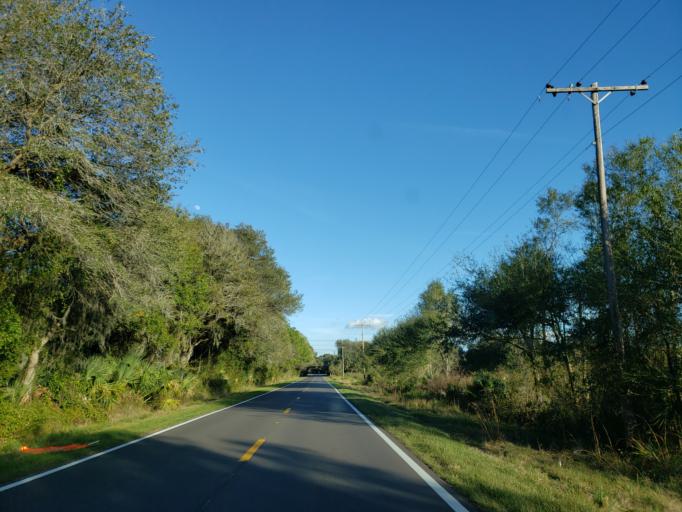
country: US
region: Florida
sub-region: Hillsborough County
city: Boyette
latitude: 27.8176
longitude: -82.2273
